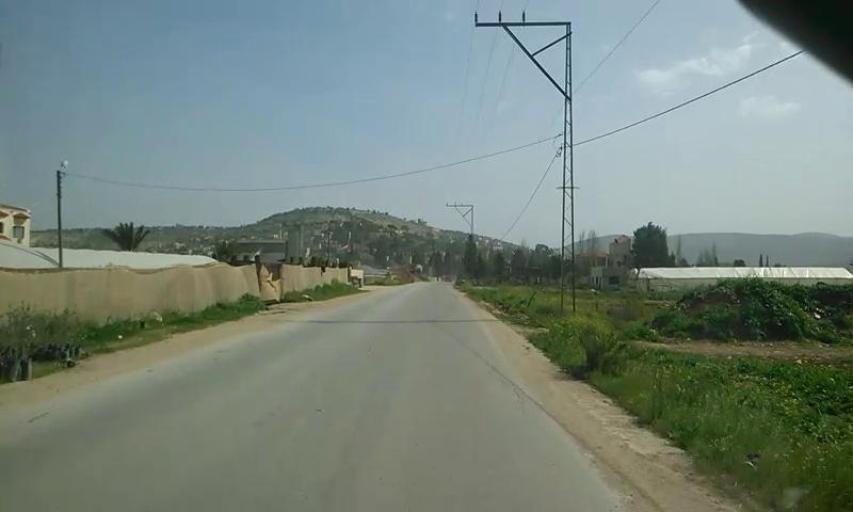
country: PS
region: West Bank
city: Ash Shuhada'
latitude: 32.4323
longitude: 35.2666
